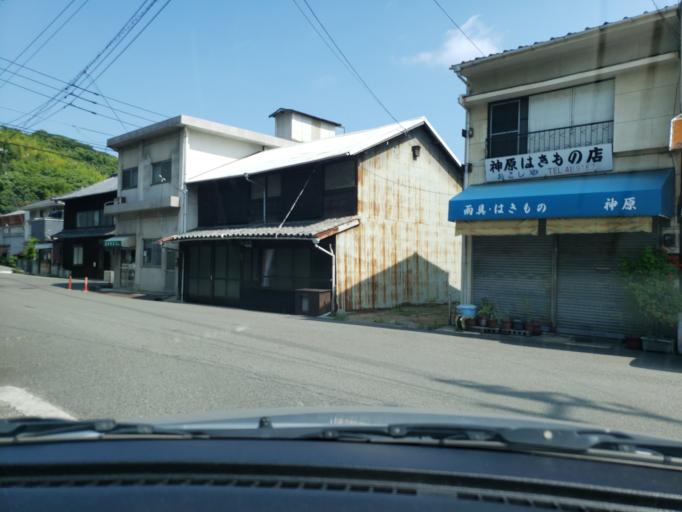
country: JP
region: Ehime
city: Hojo
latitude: 34.1060
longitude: 132.9672
